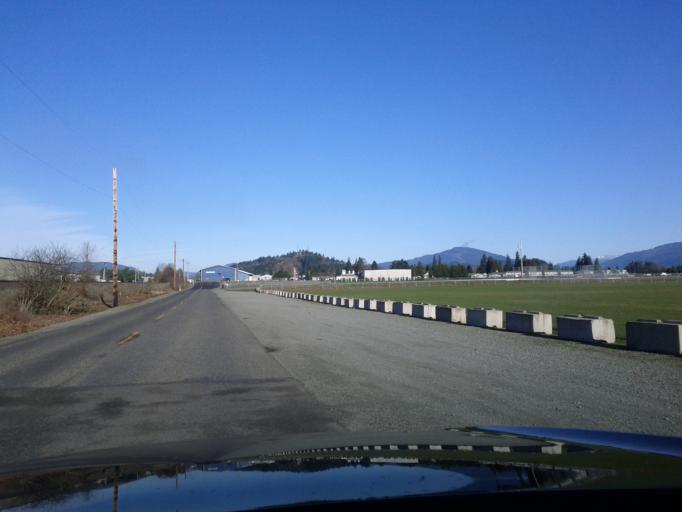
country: US
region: Washington
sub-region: Skagit County
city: Burlington
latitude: 48.4541
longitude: -122.3248
